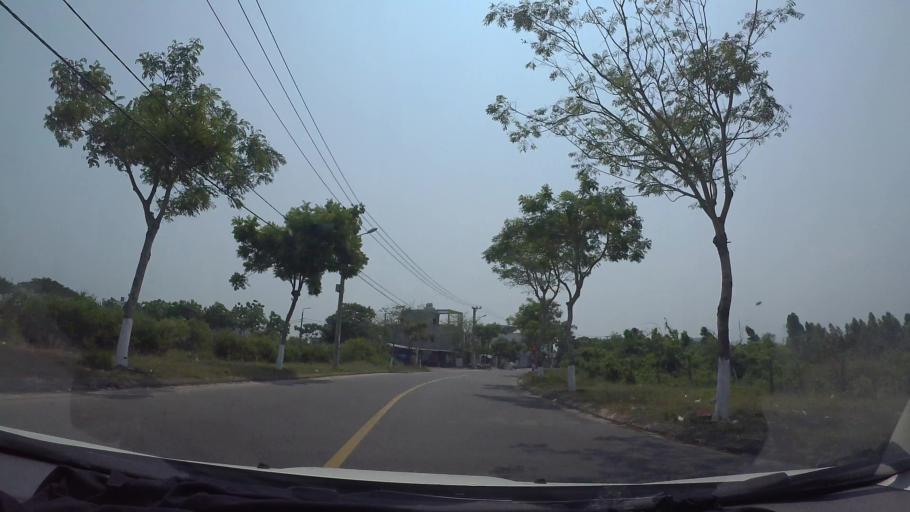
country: VN
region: Da Nang
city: Cam Le
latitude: 15.9984
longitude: 108.2023
